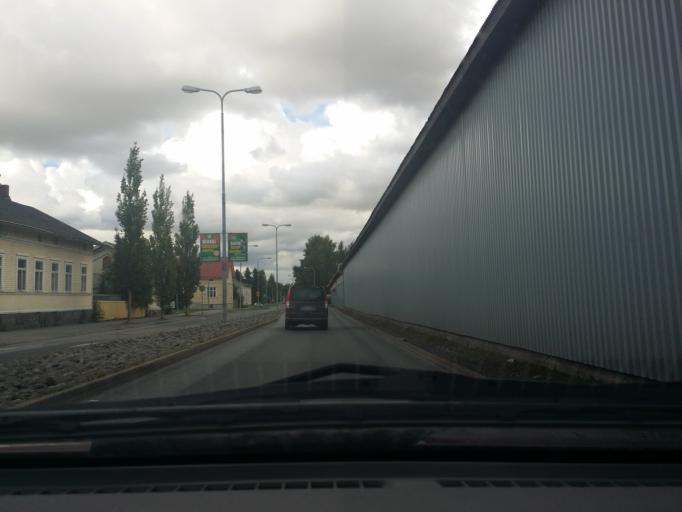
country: FI
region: Satakunta
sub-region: Pori
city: Pori
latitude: 61.4946
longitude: 21.8045
